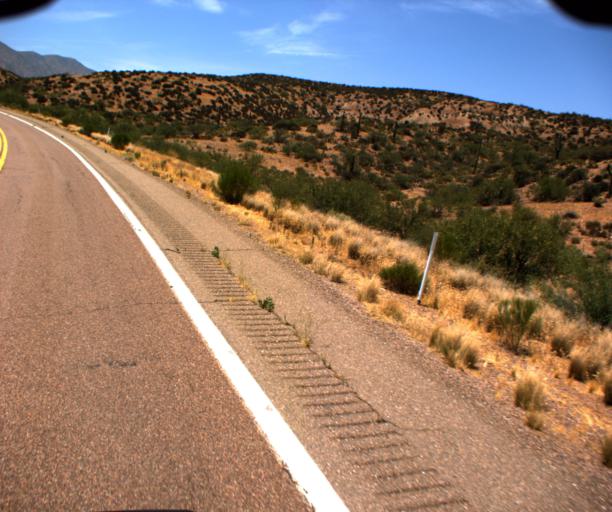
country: US
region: Arizona
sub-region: Gila County
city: Tonto Basin
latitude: 33.8038
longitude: -111.2746
